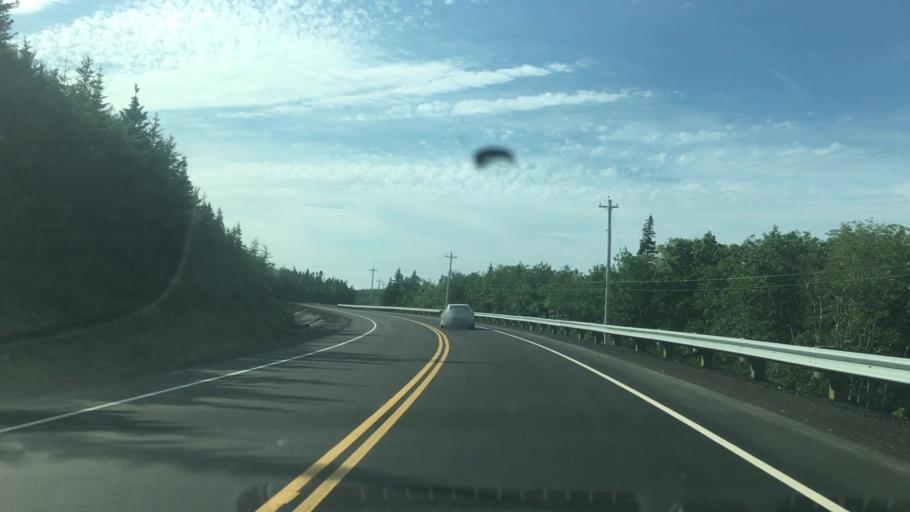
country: CA
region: Nova Scotia
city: Sydney Mines
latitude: 46.8398
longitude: -60.3883
